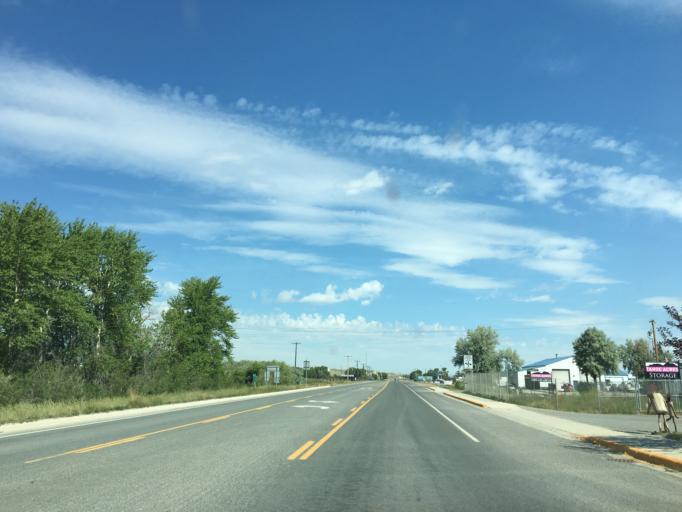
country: US
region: Montana
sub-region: Broadwater County
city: Townsend
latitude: 46.3261
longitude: -111.5260
